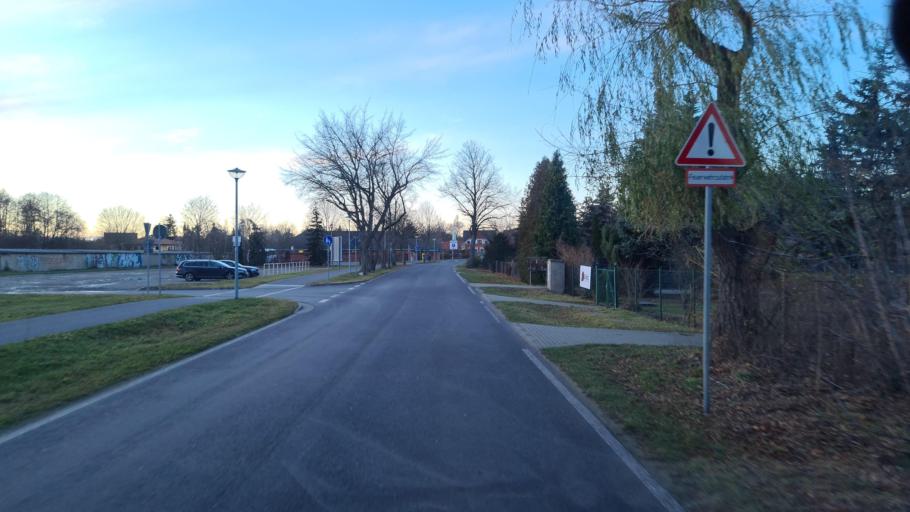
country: DE
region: Brandenburg
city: Vetschau
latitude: 51.7805
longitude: 14.0798
